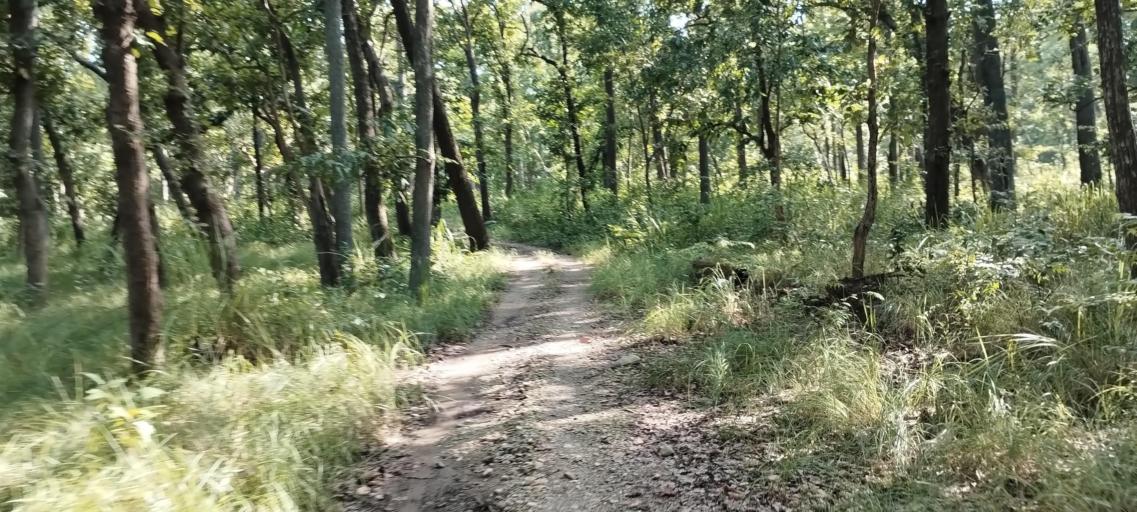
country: NP
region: Far Western
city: Tikapur
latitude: 28.5298
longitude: 81.2831
